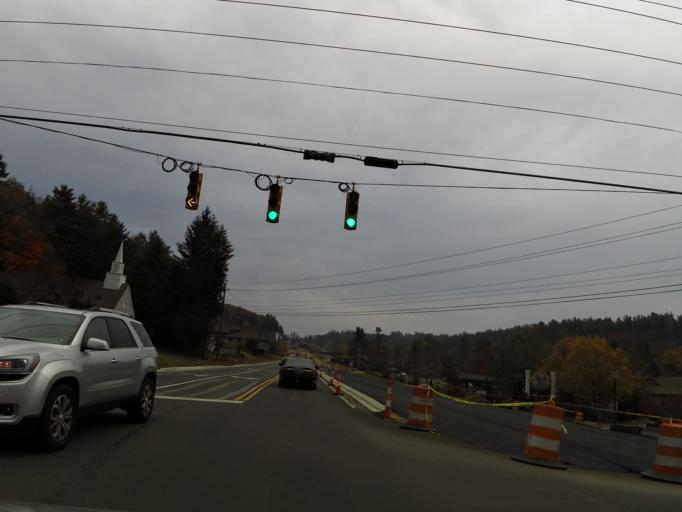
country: US
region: North Carolina
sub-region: Watauga County
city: Blowing Rock
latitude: 36.1328
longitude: -81.6713
